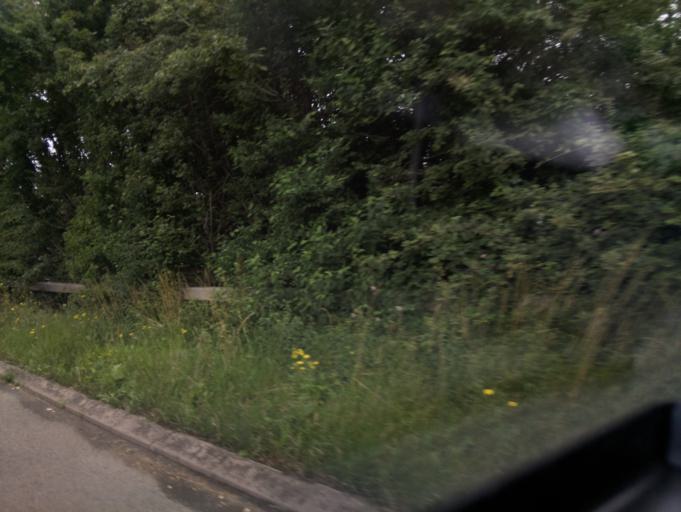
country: GB
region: England
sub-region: Gloucestershire
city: Tewkesbury
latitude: 51.9925
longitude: -2.1457
